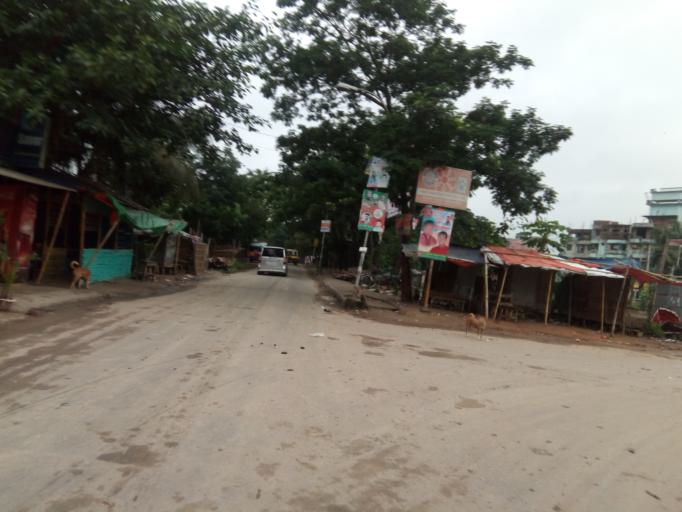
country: BD
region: Dhaka
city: Tungi
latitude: 23.8461
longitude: 90.4197
